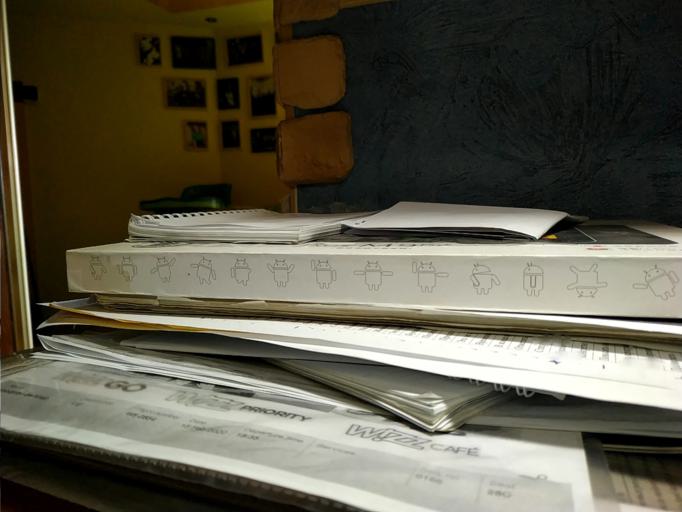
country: RU
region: Novgorod
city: Volot
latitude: 57.6888
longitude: 30.6834
